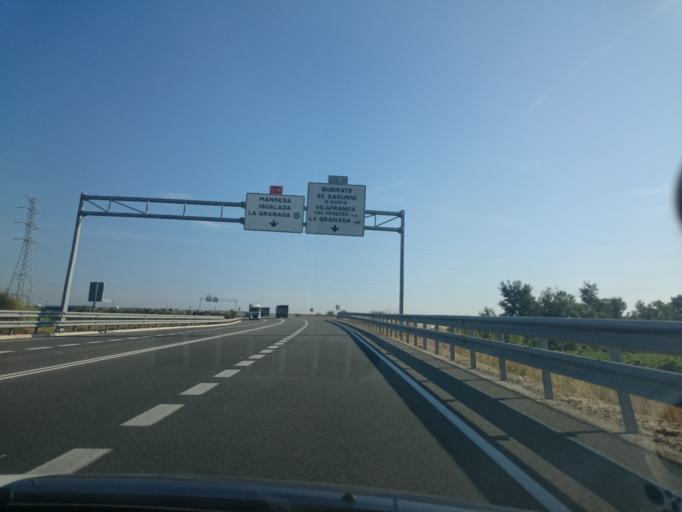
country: ES
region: Catalonia
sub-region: Provincia de Barcelona
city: La Granada
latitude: 41.3594
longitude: 1.7218
